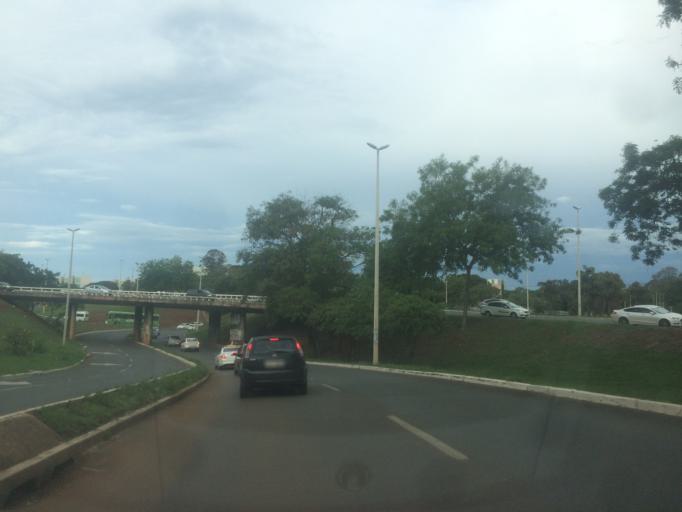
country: BR
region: Federal District
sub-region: Brasilia
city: Brasilia
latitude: -15.8031
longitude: -47.8787
